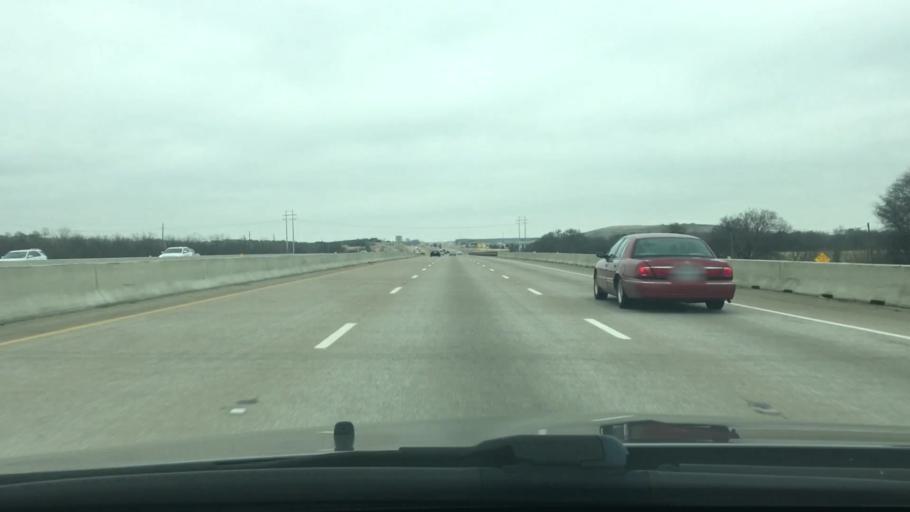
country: US
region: Texas
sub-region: Ellis County
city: Palmer
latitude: 32.4092
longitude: -96.6585
